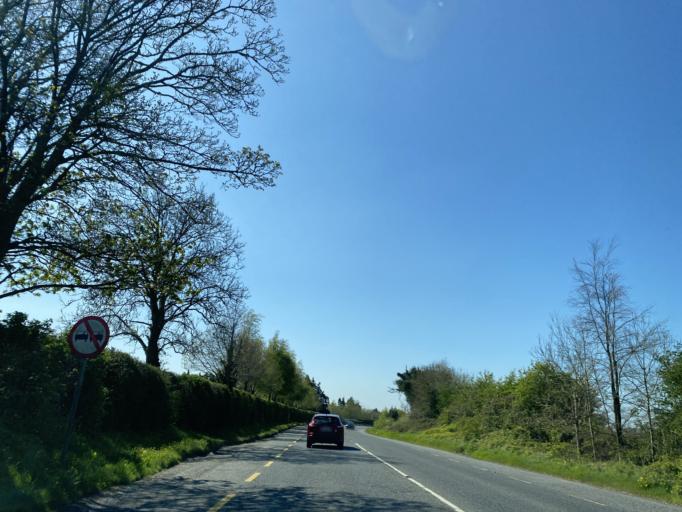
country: IE
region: Leinster
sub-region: Kildare
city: Maynooth
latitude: 53.3377
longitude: -6.6037
